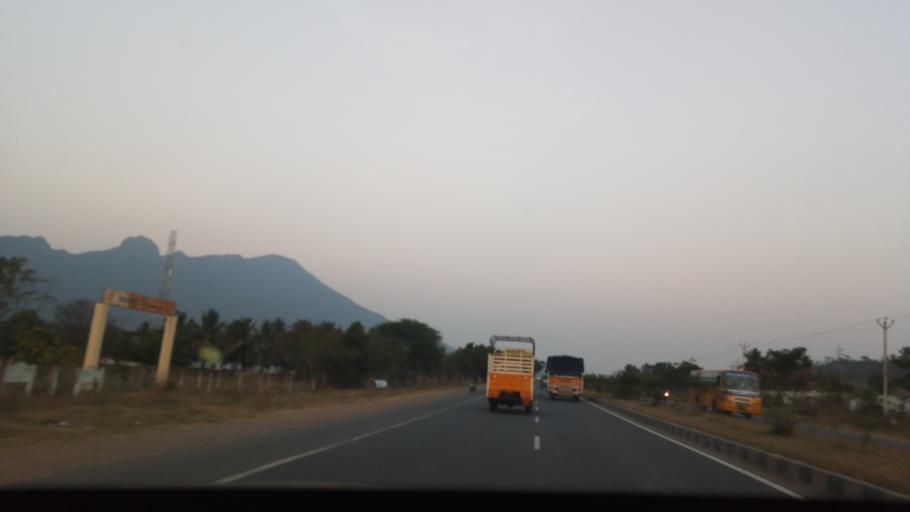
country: IN
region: Tamil Nadu
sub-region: Salem
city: Belur
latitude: 11.6658
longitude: 78.3175
